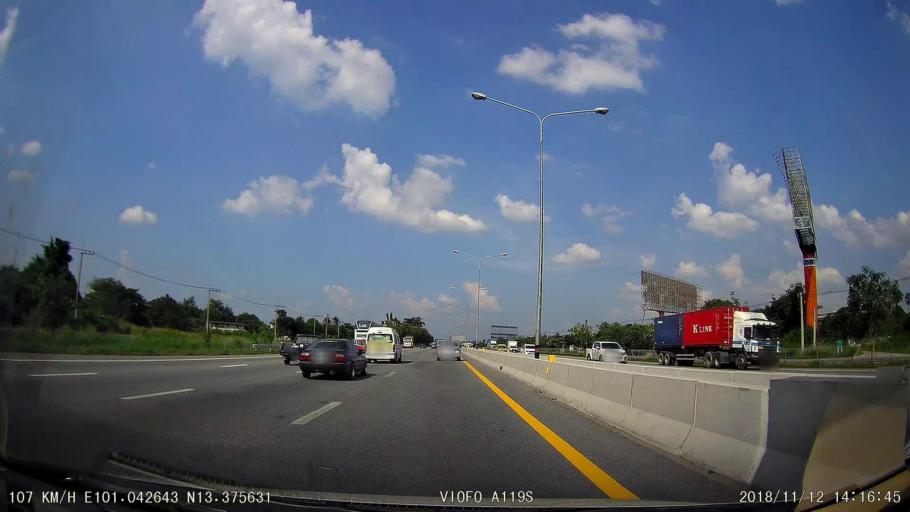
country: TH
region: Chon Buri
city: Chon Buri
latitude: 13.3758
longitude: 101.0427
